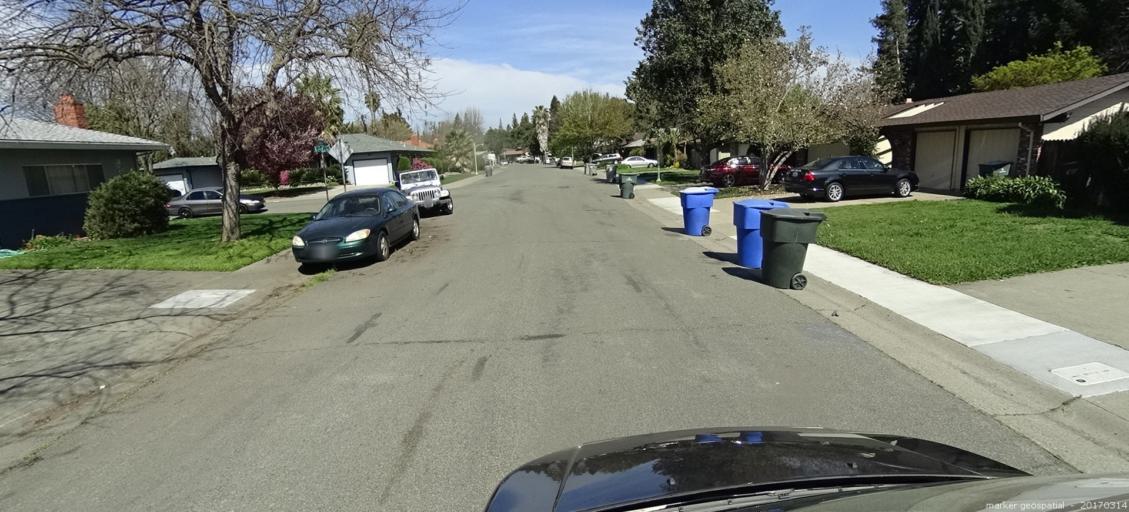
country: US
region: California
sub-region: Sacramento County
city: Parkway
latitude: 38.5120
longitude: -121.5231
